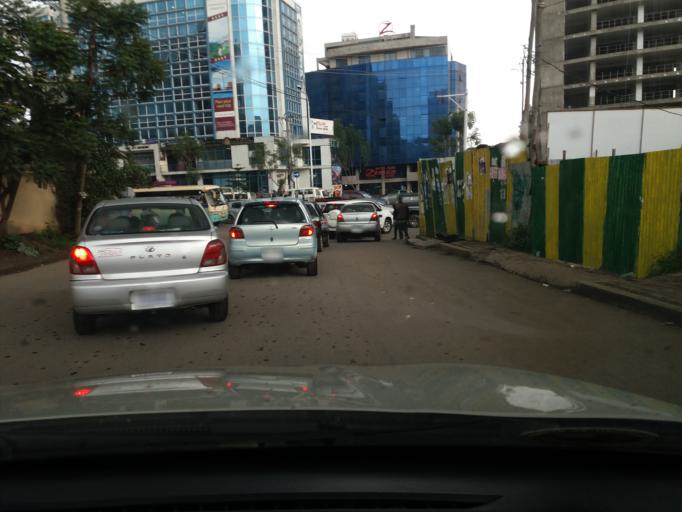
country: ET
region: Adis Abeba
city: Addis Ababa
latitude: 8.9910
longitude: 38.7848
